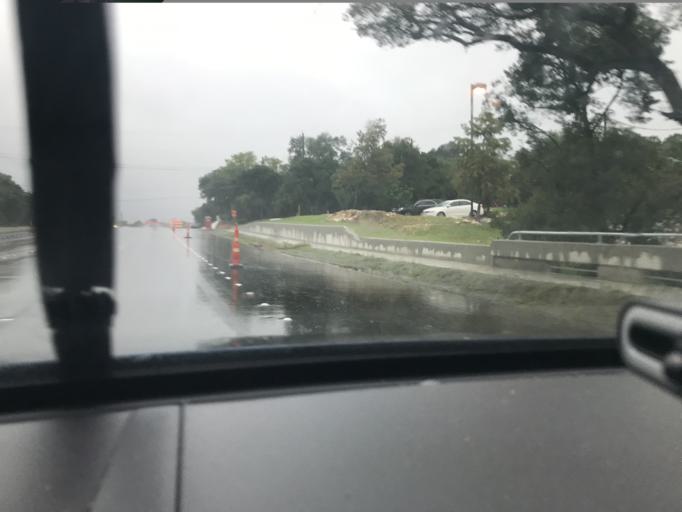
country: US
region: Texas
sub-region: Travis County
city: West Lake Hills
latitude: 30.2887
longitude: -97.8171
